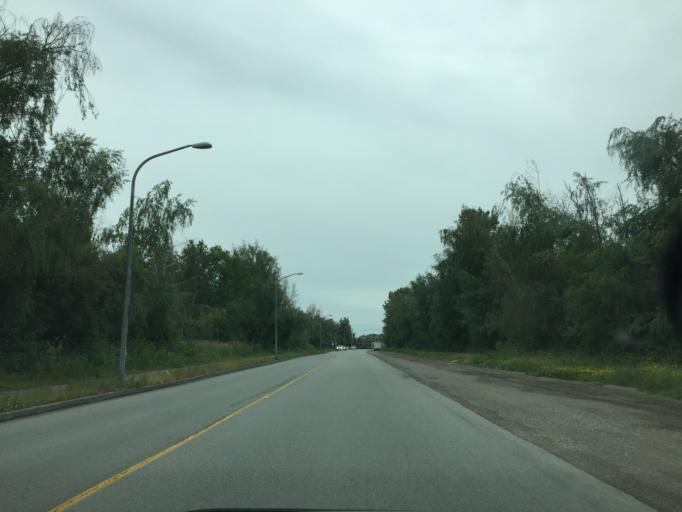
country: CA
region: British Columbia
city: Richmond
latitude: 49.1729
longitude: -123.1030
